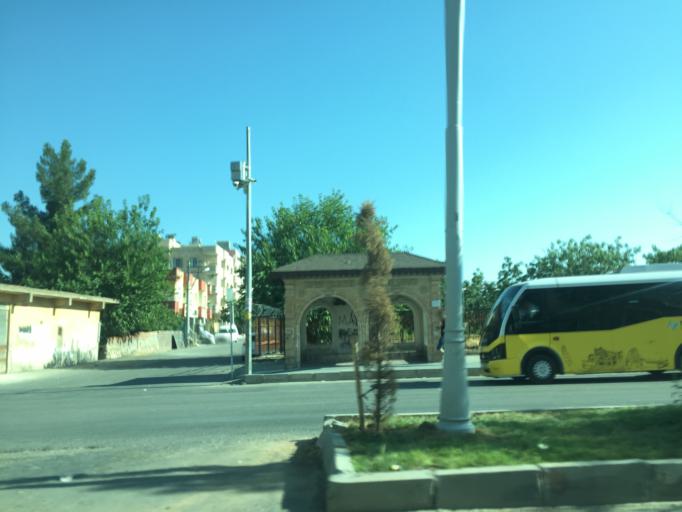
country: TR
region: Mardin
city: Midyat
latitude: 37.4162
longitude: 41.3672
